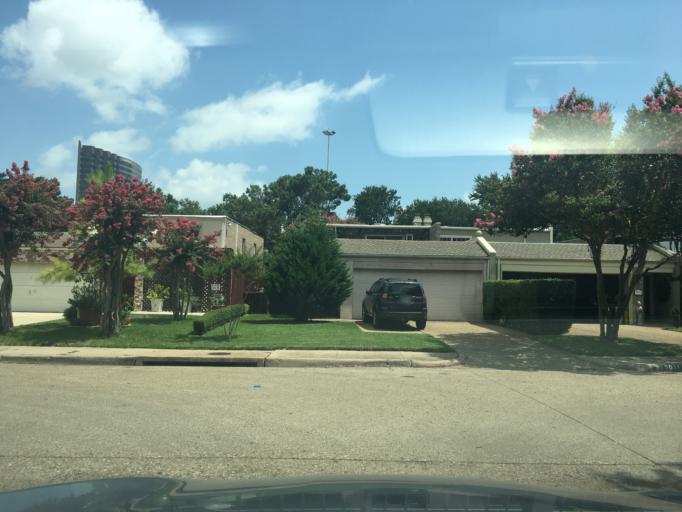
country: US
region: Texas
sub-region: Dallas County
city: Addison
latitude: 32.9235
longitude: -96.8215
